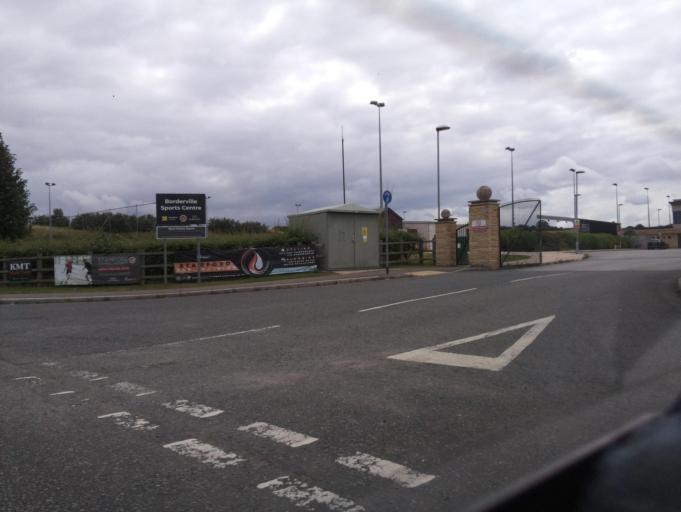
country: GB
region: England
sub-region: District of Rutland
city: Ryhall
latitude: 52.6663
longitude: -0.4678
